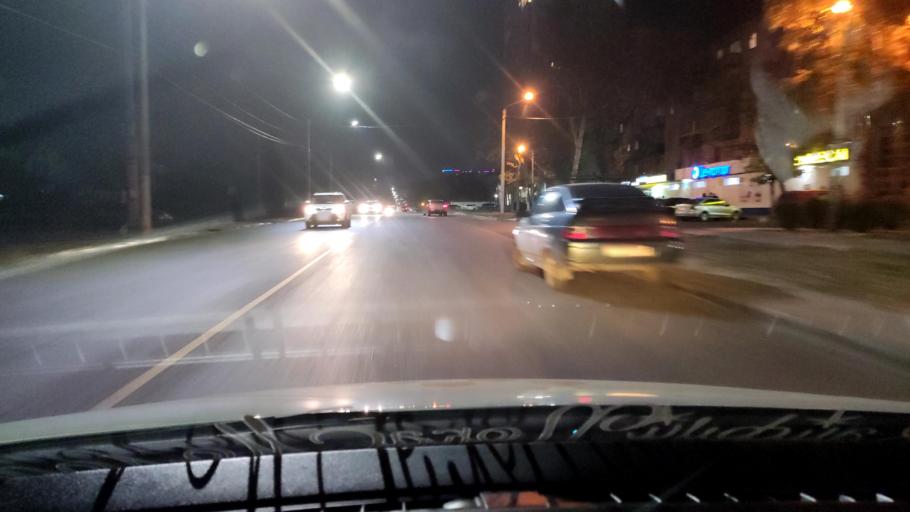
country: RU
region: Voronezj
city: Voronezh
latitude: 51.6370
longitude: 39.1730
